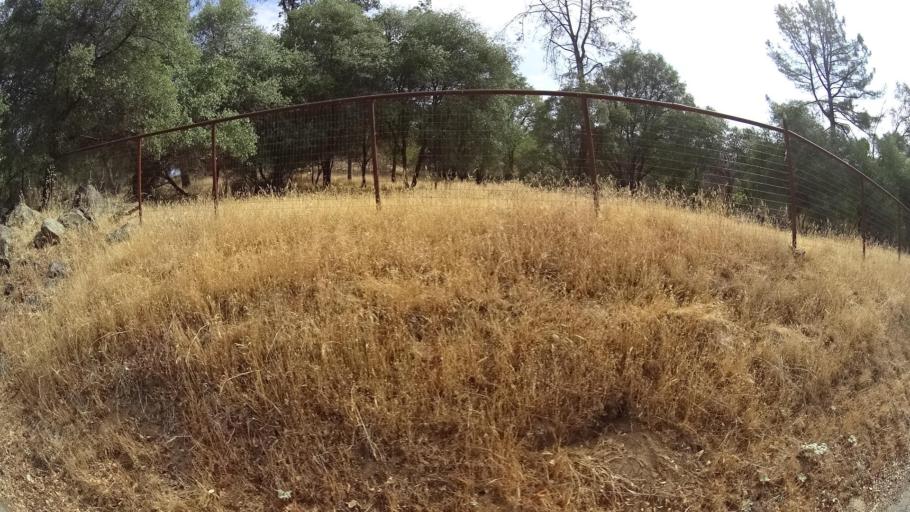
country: US
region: California
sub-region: Mariposa County
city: Midpines
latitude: 37.5115
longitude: -119.8916
